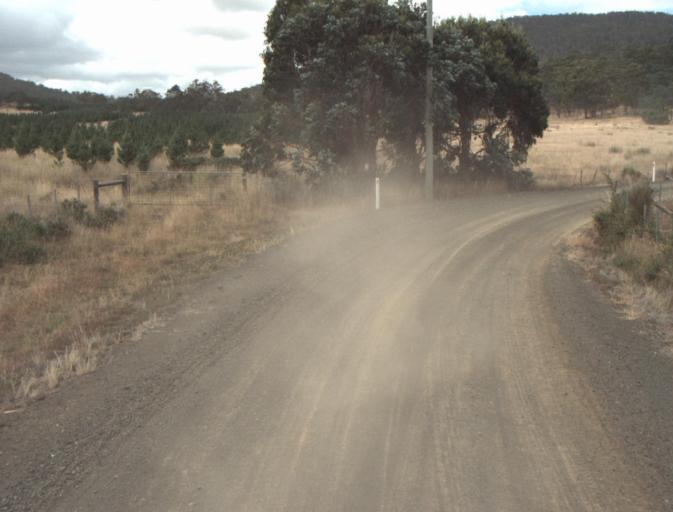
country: AU
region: Tasmania
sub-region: Northern Midlands
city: Evandale
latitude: -41.5133
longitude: 147.3826
